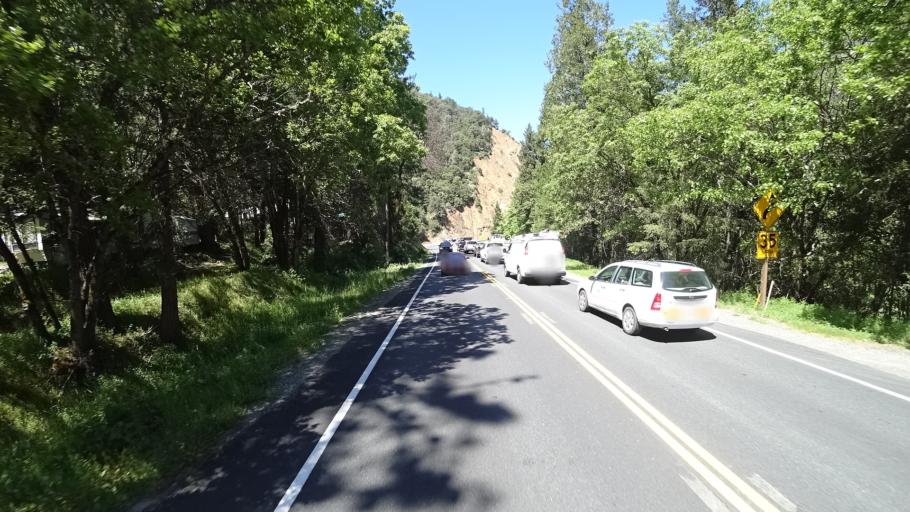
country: US
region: California
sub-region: Humboldt County
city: Willow Creek
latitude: 40.8117
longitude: -123.4782
